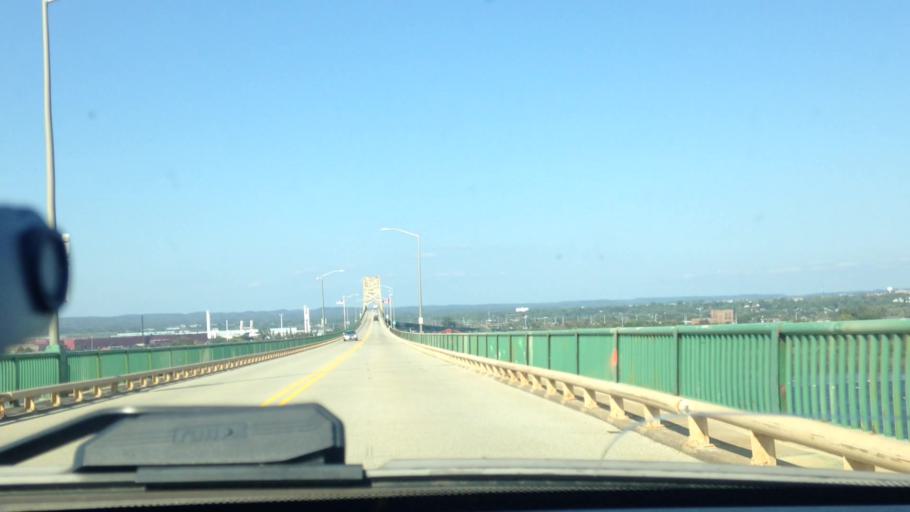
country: US
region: Michigan
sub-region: Chippewa County
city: Sault Ste. Marie
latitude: 46.5064
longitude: -84.3620
